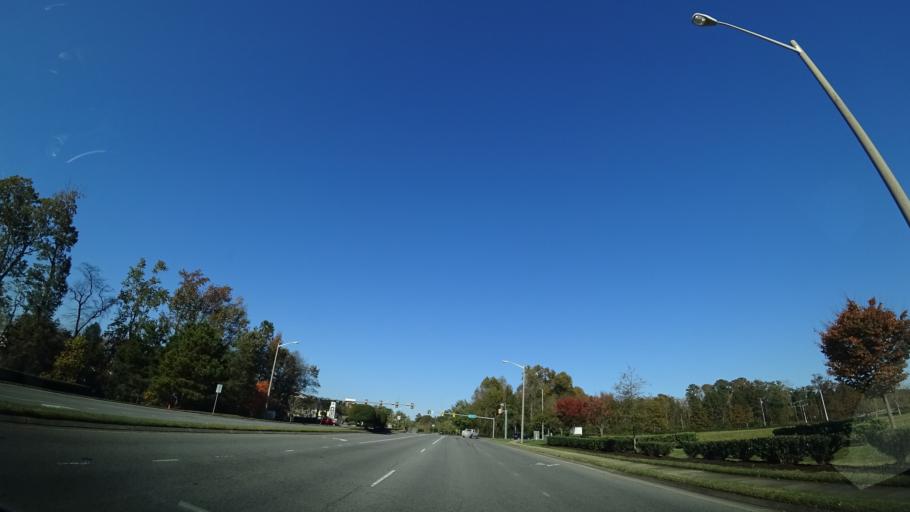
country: US
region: Virginia
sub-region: City of Portsmouth
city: Portsmouth Heights
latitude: 36.8756
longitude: -76.4385
